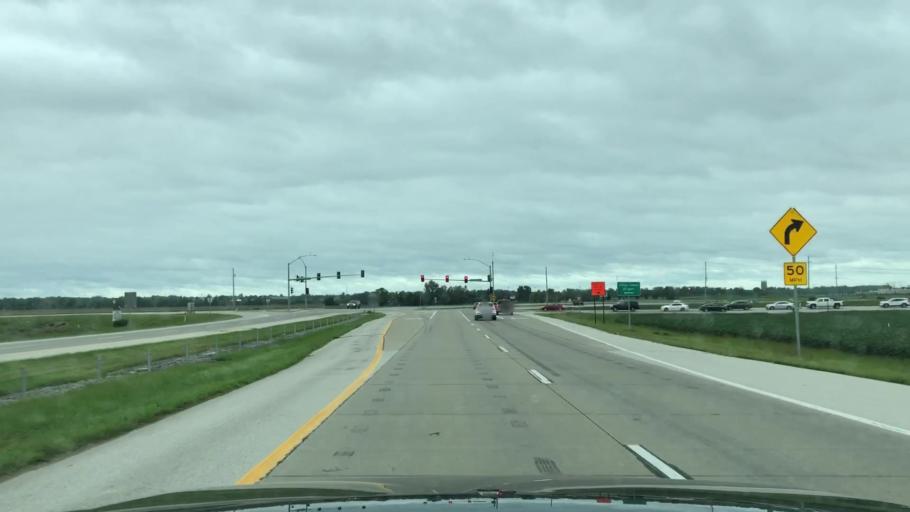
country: US
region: Missouri
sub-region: Saint Charles County
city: Saint Charles
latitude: 38.7236
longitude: -90.4983
